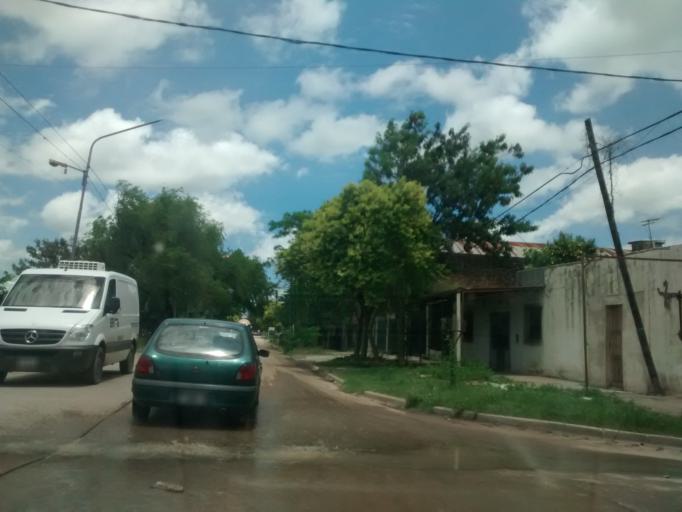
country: AR
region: Chaco
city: Fontana
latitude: -27.4340
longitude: -59.0013
